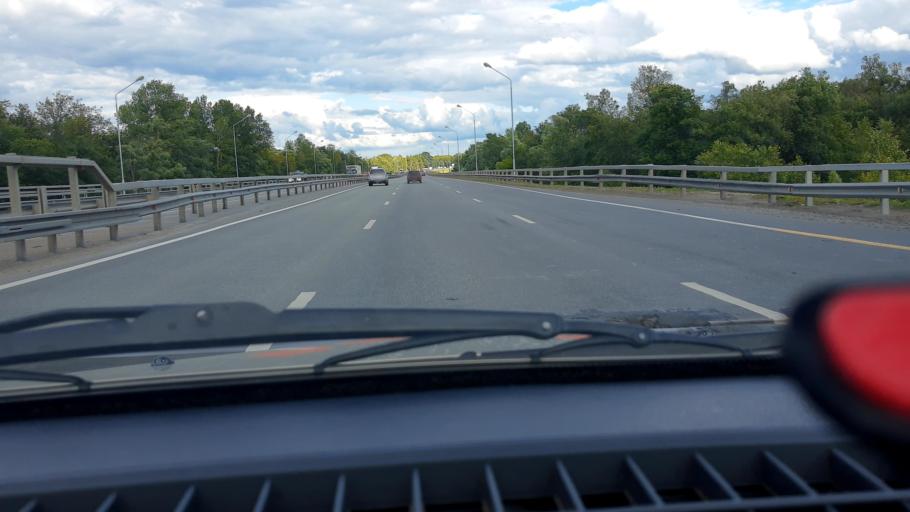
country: RU
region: Bashkortostan
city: Ufa
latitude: 54.6614
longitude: 55.8751
